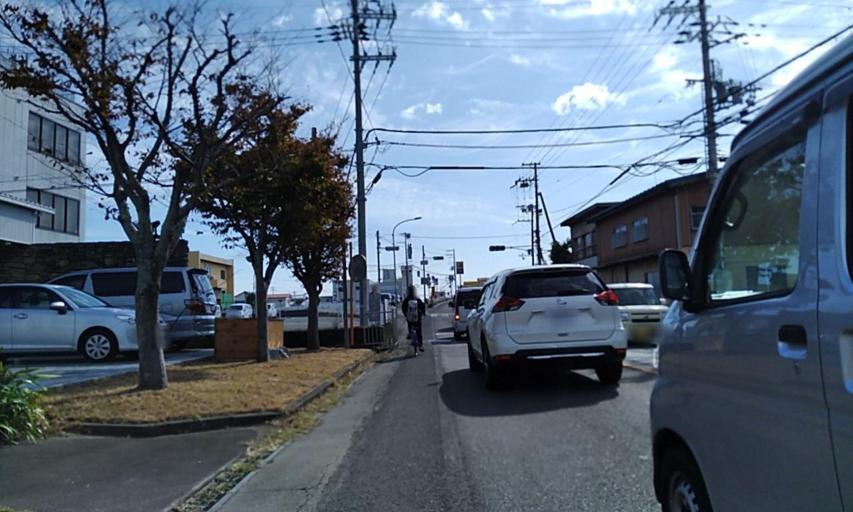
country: JP
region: Wakayama
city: Gobo
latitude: 33.9073
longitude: 135.1511
